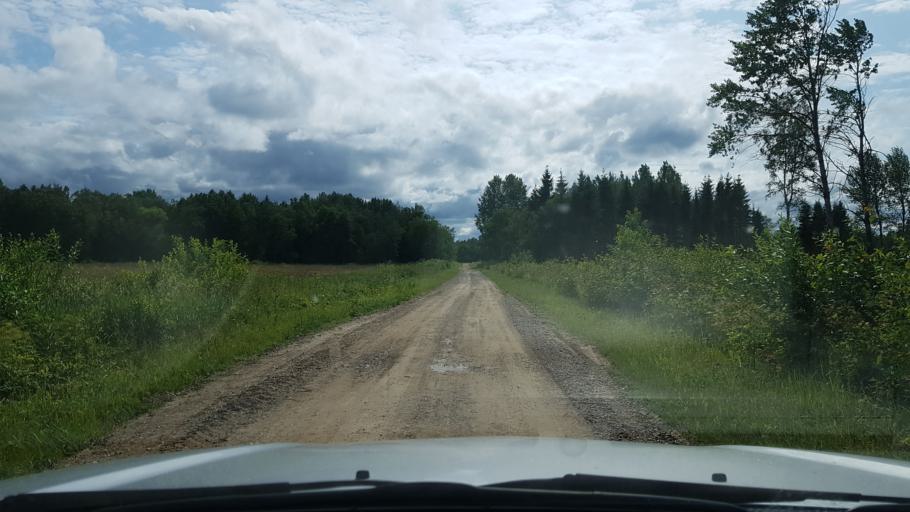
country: EE
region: Ida-Virumaa
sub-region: Narva-Joesuu linn
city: Narva-Joesuu
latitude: 59.3668
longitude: 27.9252
